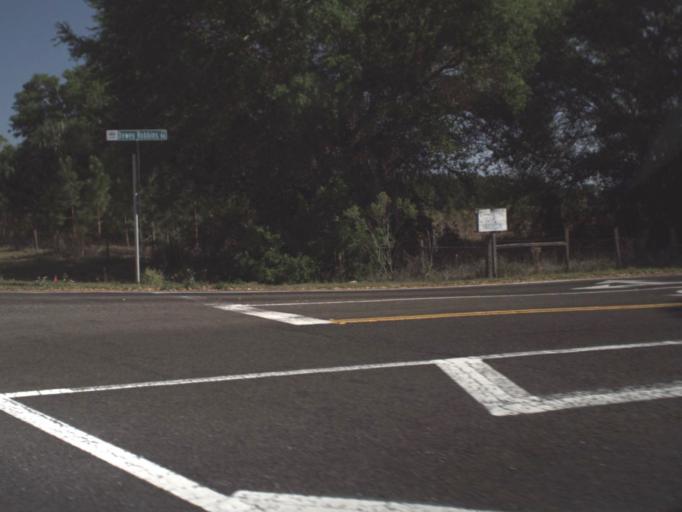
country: US
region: Florida
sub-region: Lake County
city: Yalaha
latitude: 28.6964
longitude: -81.8569
